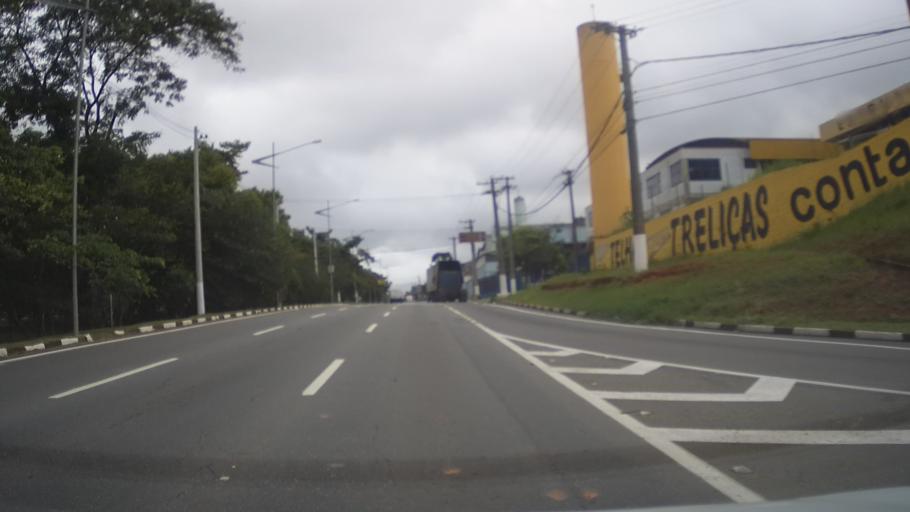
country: BR
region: Sao Paulo
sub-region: Aruja
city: Aruja
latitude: -23.4049
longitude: -46.3304
